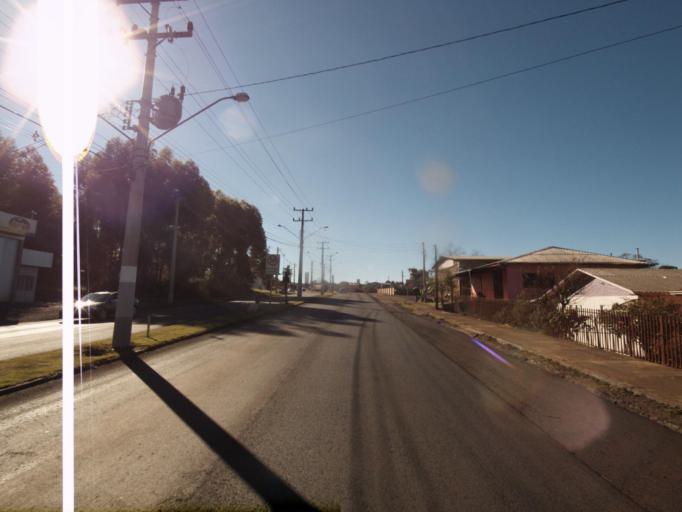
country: AR
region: Misiones
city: Bernardo de Irigoyen
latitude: -26.7400
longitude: -53.5012
